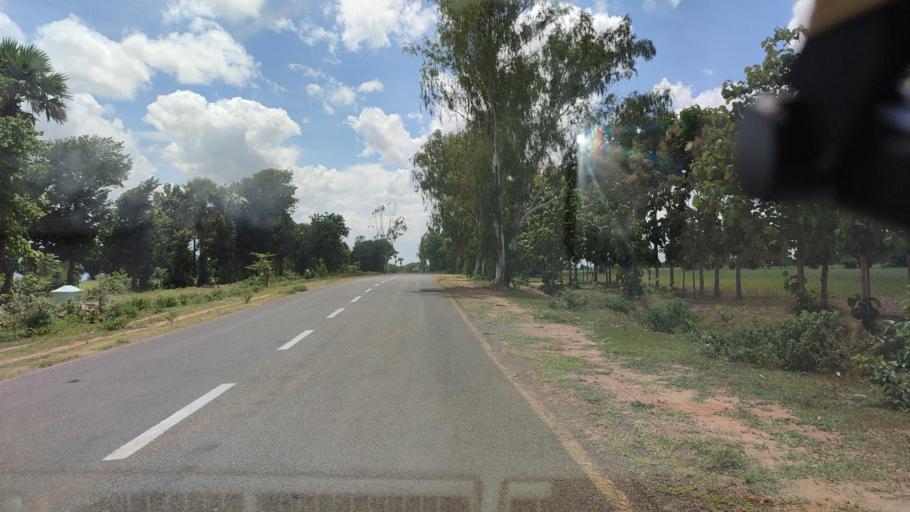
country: MM
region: Magway
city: Magway
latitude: 20.1894
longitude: 95.0444
